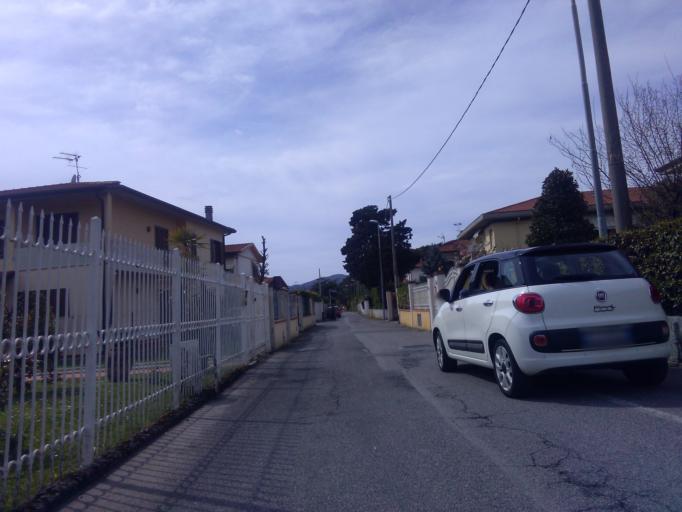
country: IT
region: Tuscany
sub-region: Provincia di Massa-Carrara
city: Marina di Carrara
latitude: 44.0482
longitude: 10.0313
